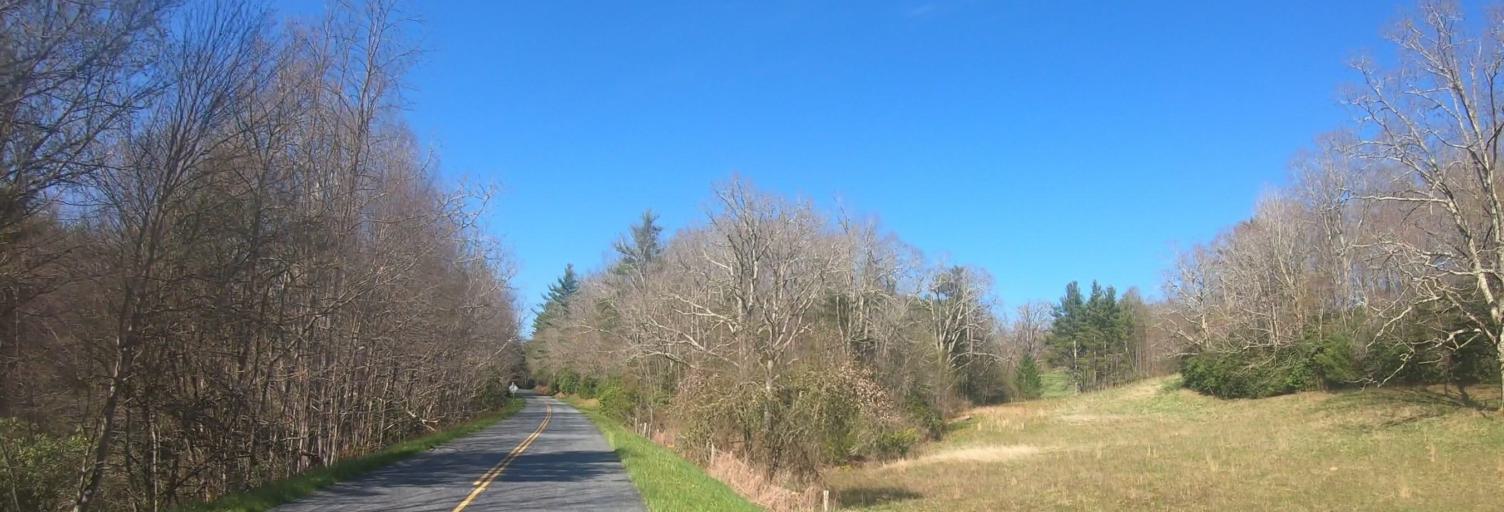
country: US
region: North Carolina
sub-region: Avery County
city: Newland
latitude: 36.0116
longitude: -81.8861
